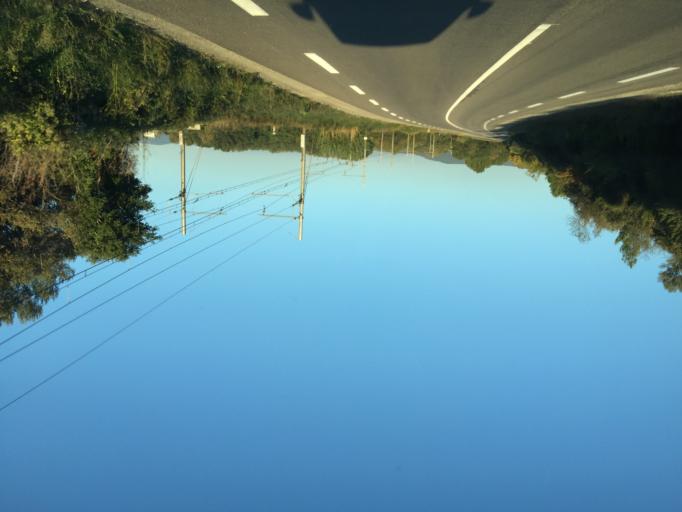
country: FR
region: Rhone-Alpes
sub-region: Departement de la Drome
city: Donzere
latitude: 44.4391
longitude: 4.6760
